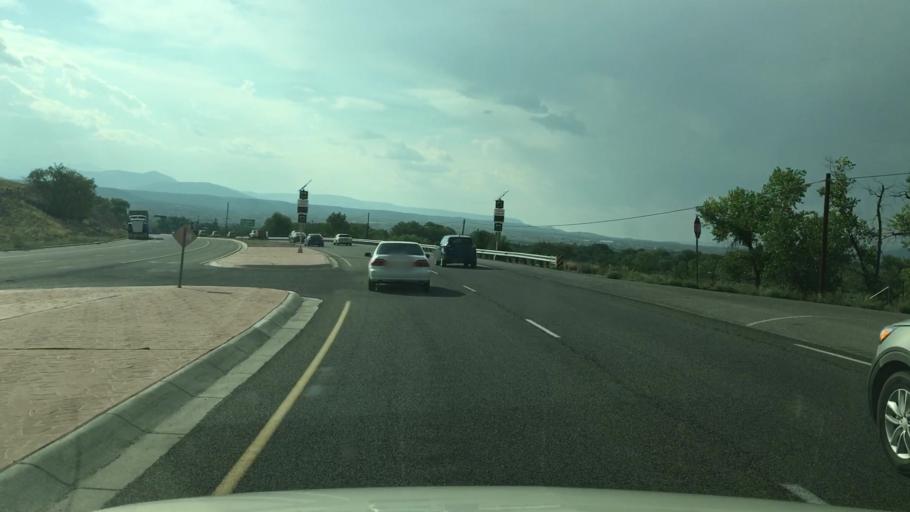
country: US
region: New Mexico
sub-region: Rio Arriba County
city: Espanola
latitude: 35.9855
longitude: -106.0527
